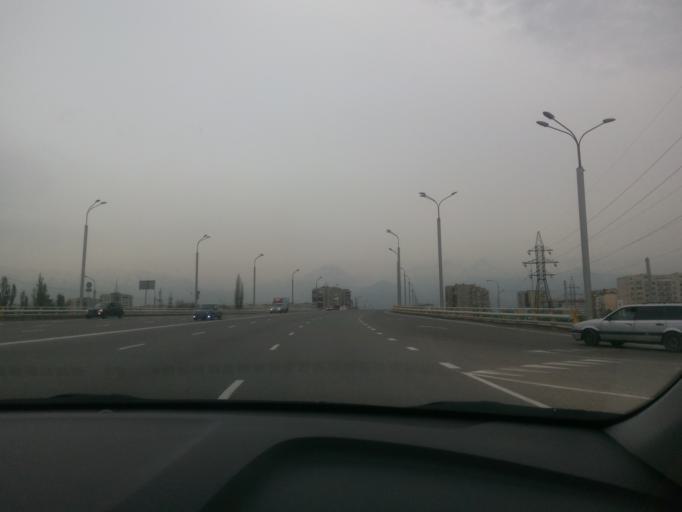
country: KZ
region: Almaty Qalasy
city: Almaty
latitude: 43.2451
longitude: 76.8272
